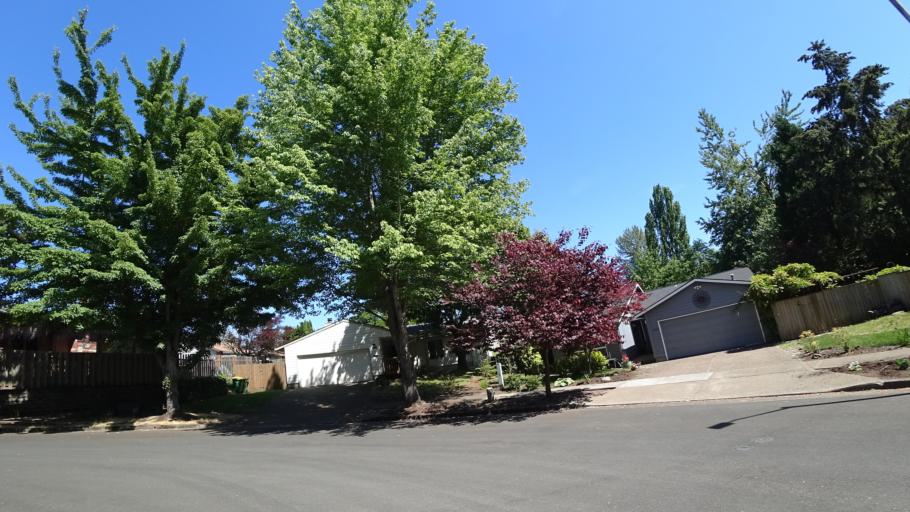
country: US
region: Oregon
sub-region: Washington County
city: Tigard
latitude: 45.4461
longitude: -122.8074
